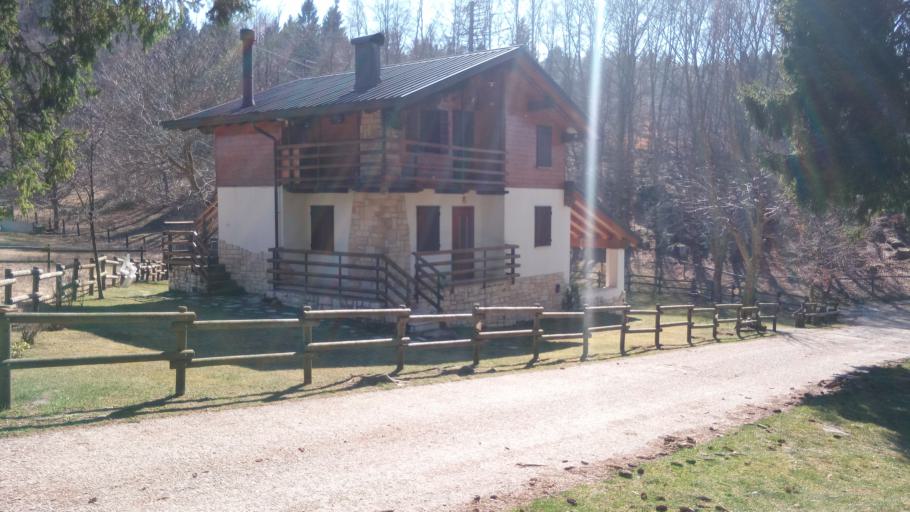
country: IT
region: Veneto
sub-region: Provincia di Treviso
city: Borso del Grappa
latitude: 45.8368
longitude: 11.7789
